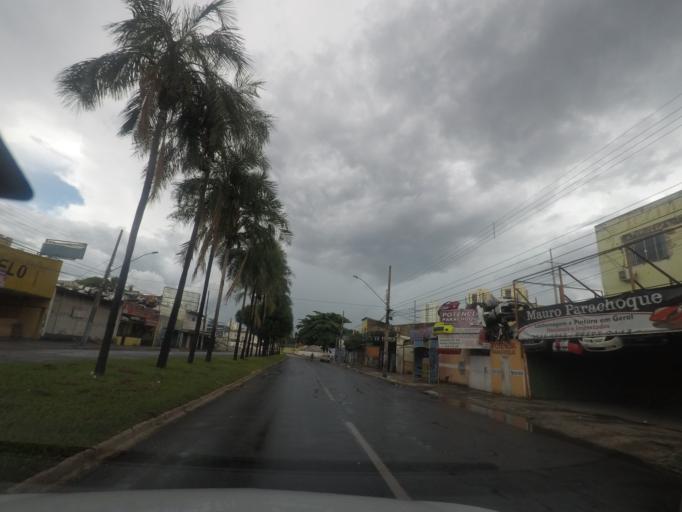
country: BR
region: Goias
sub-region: Goiania
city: Goiania
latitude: -16.6698
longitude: -49.2747
